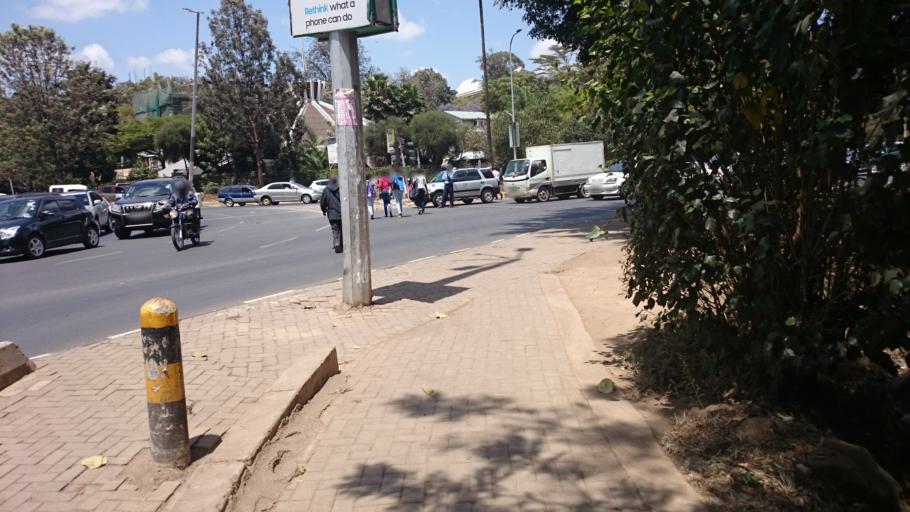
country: KE
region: Nairobi Area
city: Nairobi
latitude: -1.2815
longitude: 36.8152
